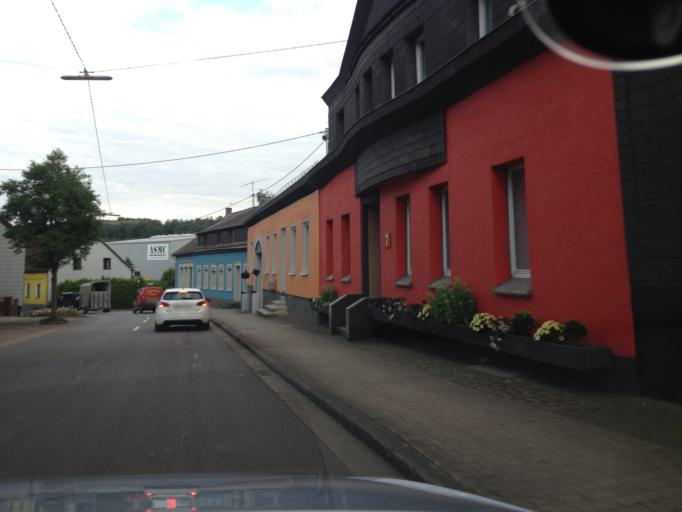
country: DE
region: Saarland
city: Friedrichsthal
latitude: 49.3517
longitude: 7.0989
